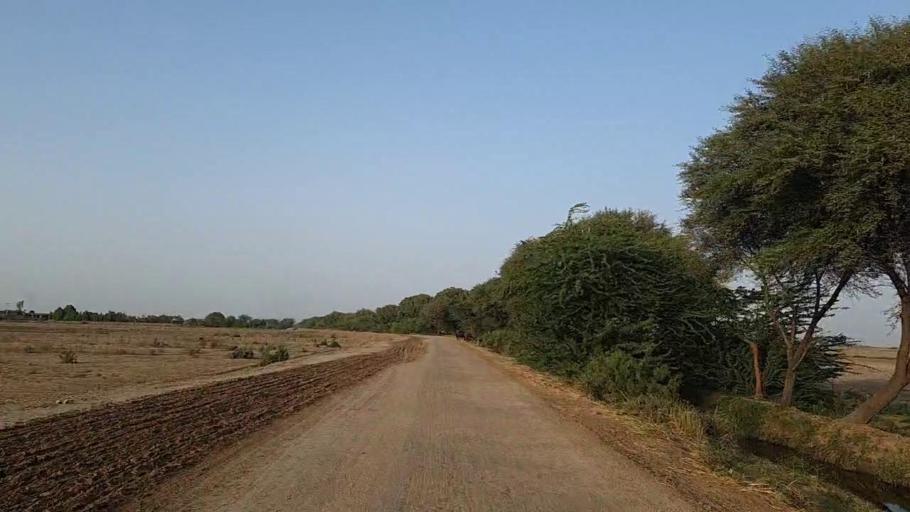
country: PK
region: Sindh
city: Jati
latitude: 24.4156
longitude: 68.1890
